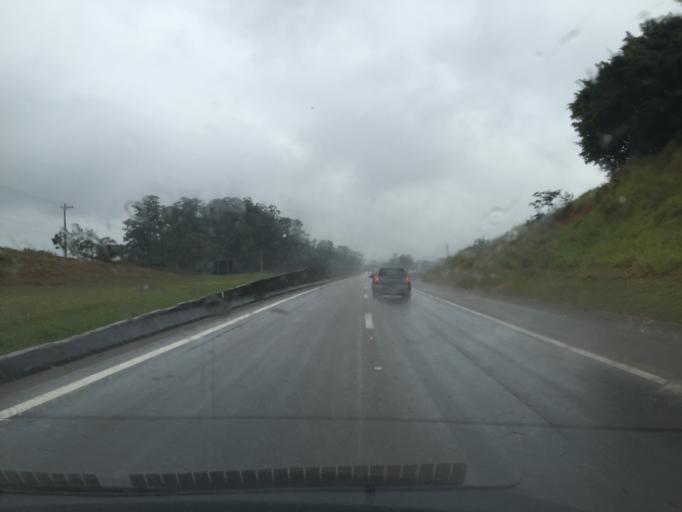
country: BR
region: Sao Paulo
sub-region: Itu
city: Itu
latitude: -23.3806
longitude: -47.3277
